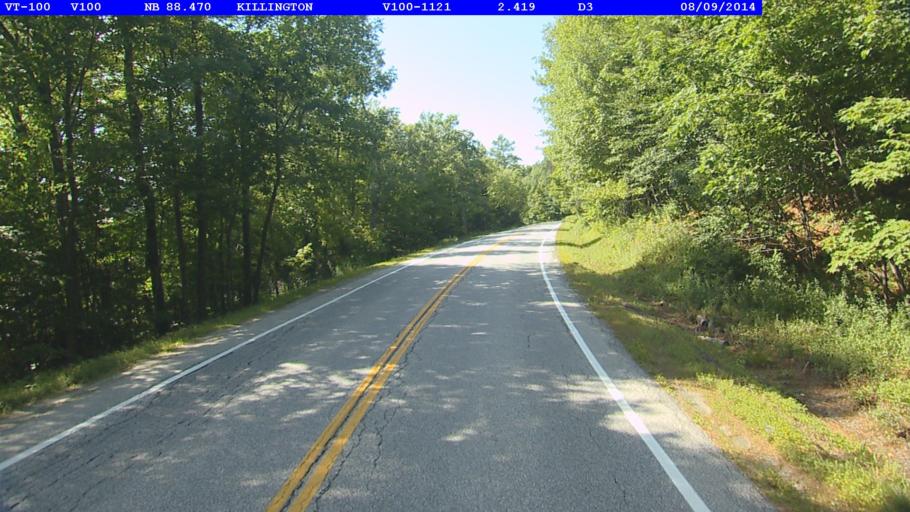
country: US
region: Vermont
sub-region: Rutland County
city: Rutland
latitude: 43.6993
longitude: -72.8158
